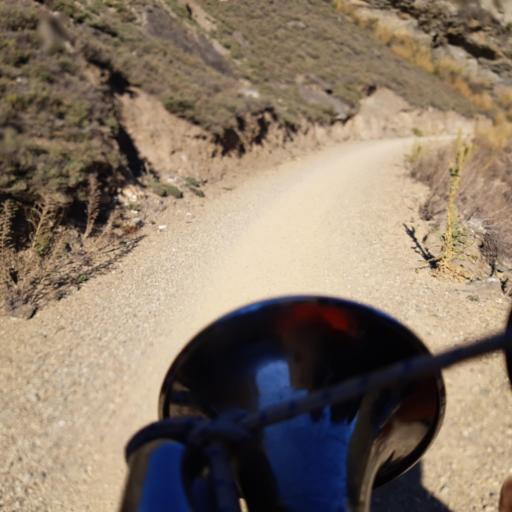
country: NZ
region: Otago
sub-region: Queenstown-Lakes District
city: Wanaka
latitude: -45.1073
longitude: 169.2931
